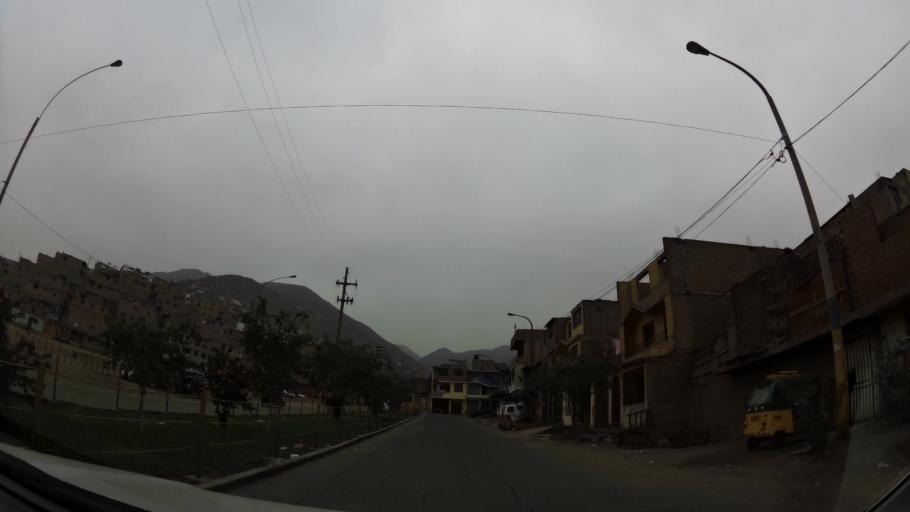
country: PE
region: Lima
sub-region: Lima
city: Independencia
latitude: -11.9684
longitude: -77.0116
